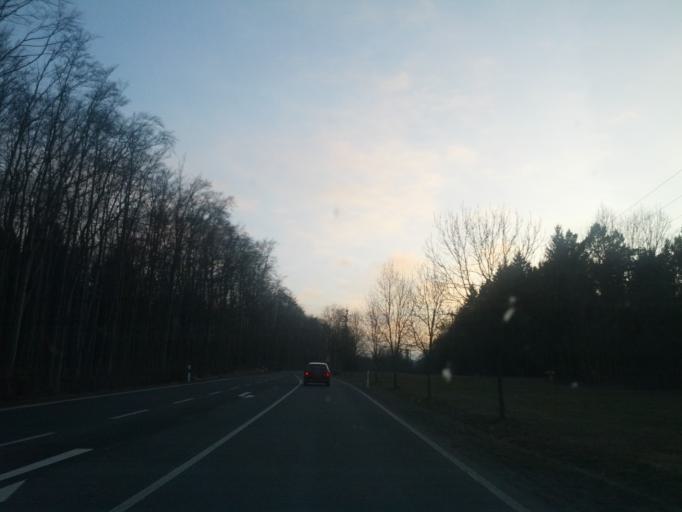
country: DE
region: Thuringia
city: Heyerode
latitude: 51.2018
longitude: 10.3168
